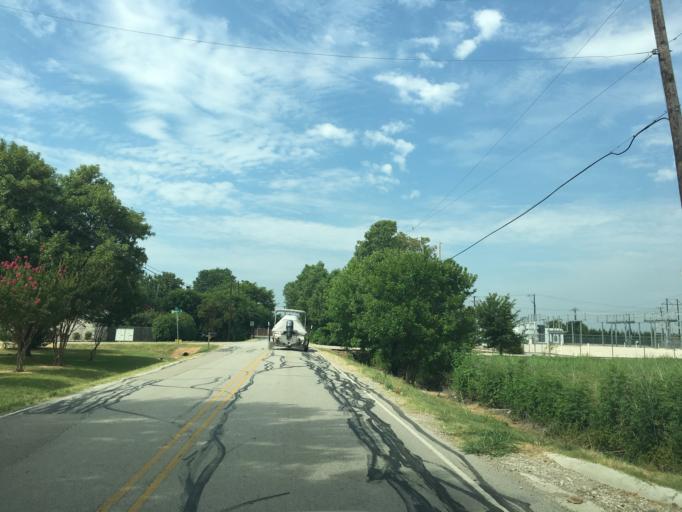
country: US
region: Texas
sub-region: Collin County
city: Wylie
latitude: 32.9625
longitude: -96.5312
